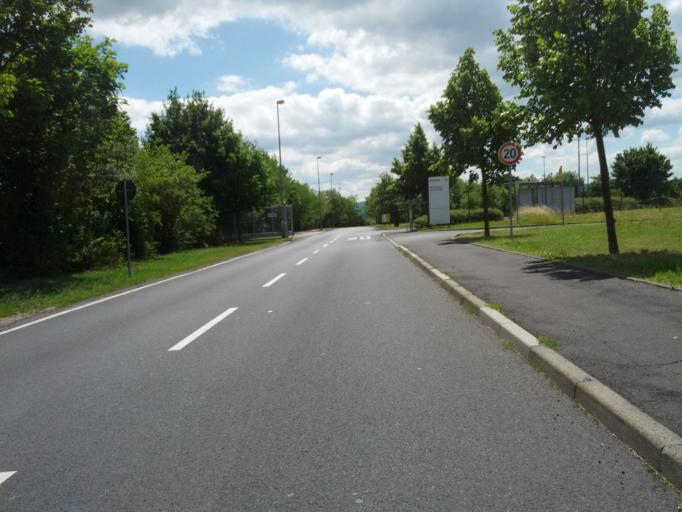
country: DE
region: Thuringia
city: Eisenach
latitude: 50.9918
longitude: 10.3498
